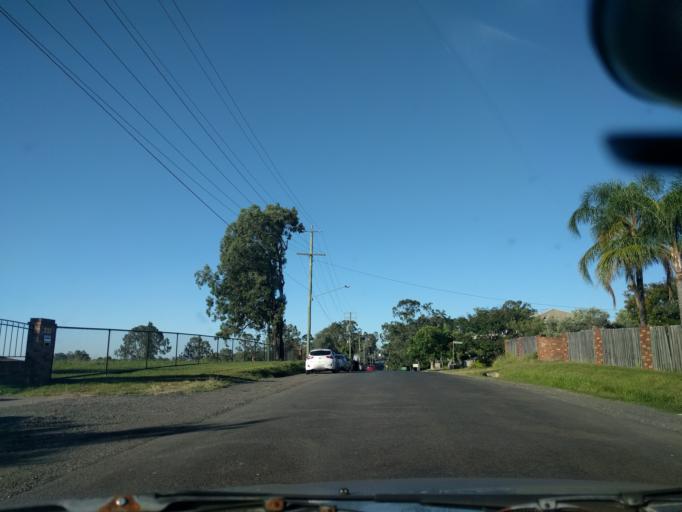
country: AU
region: Queensland
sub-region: Brisbane
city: Richlands
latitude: -27.6013
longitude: 152.9483
